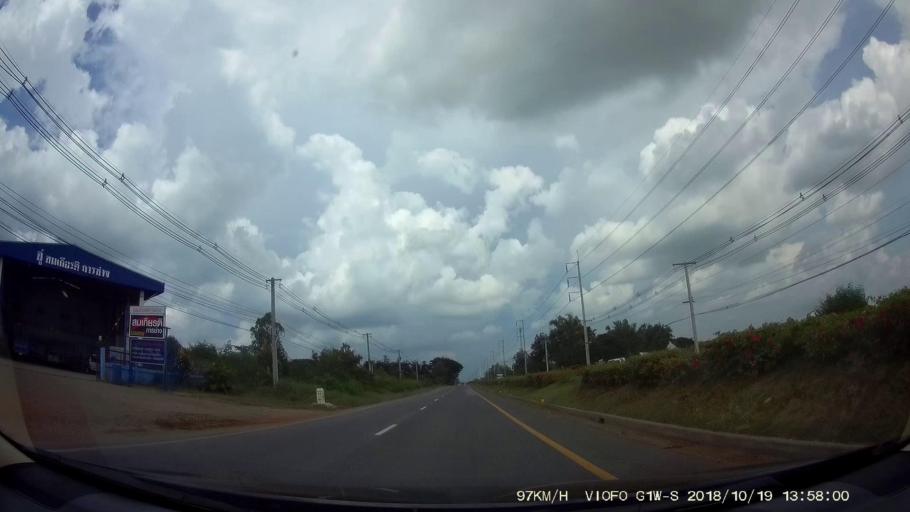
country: TH
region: Chaiyaphum
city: Chaiyaphum
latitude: 15.7941
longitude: 102.0490
